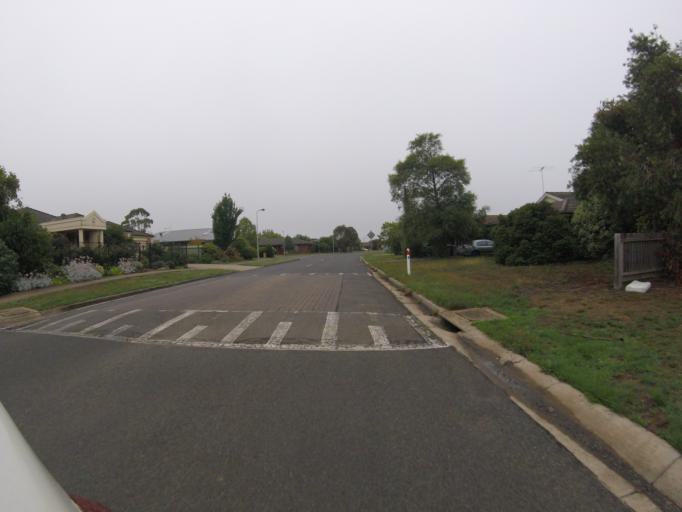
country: AU
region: Victoria
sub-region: Ballarat North
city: Newington
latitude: -37.5506
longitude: 143.7966
